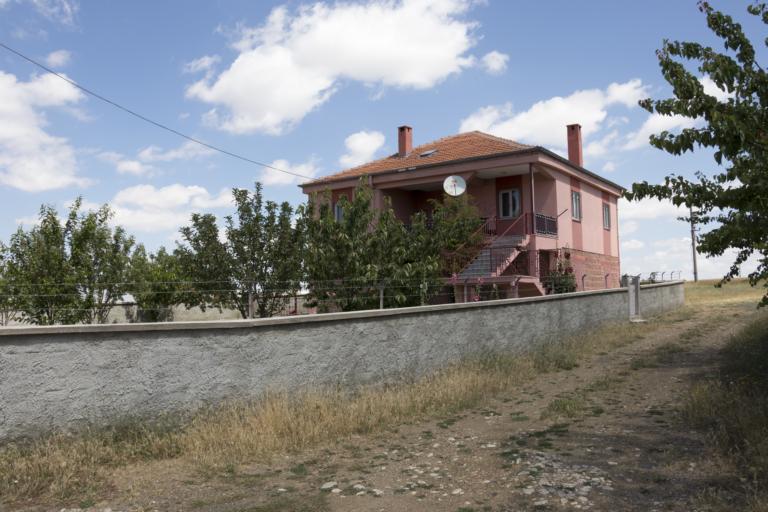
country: TR
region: Kayseri
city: Toklar
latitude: 38.4079
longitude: 36.0758
